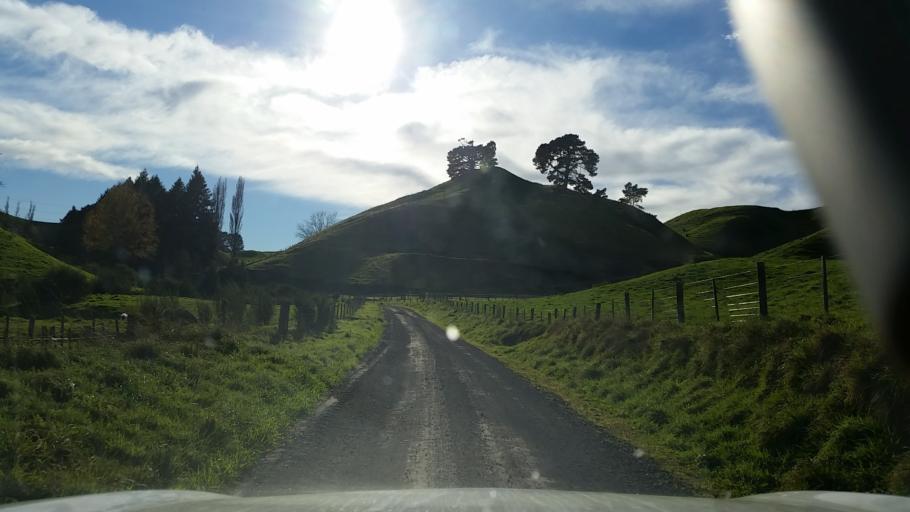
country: NZ
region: Waikato
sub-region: South Waikato District
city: Tokoroa
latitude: -38.3698
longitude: 176.0882
